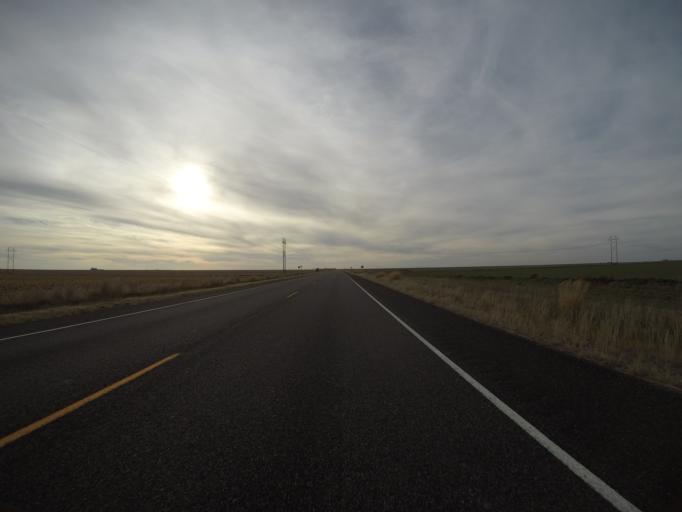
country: US
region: Colorado
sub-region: Yuma County
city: Wray
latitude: 39.7460
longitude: -102.1435
